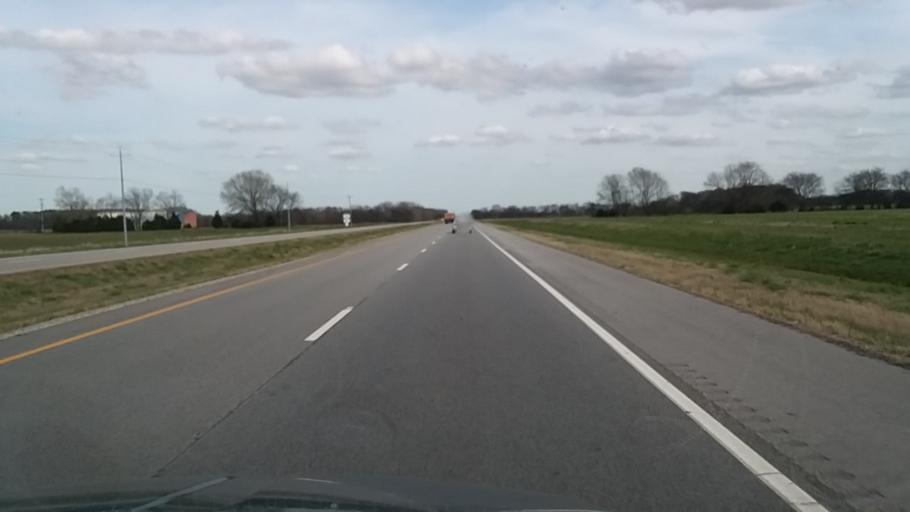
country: US
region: Alabama
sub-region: Lawrence County
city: Town Creek
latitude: 34.6837
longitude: -87.5229
